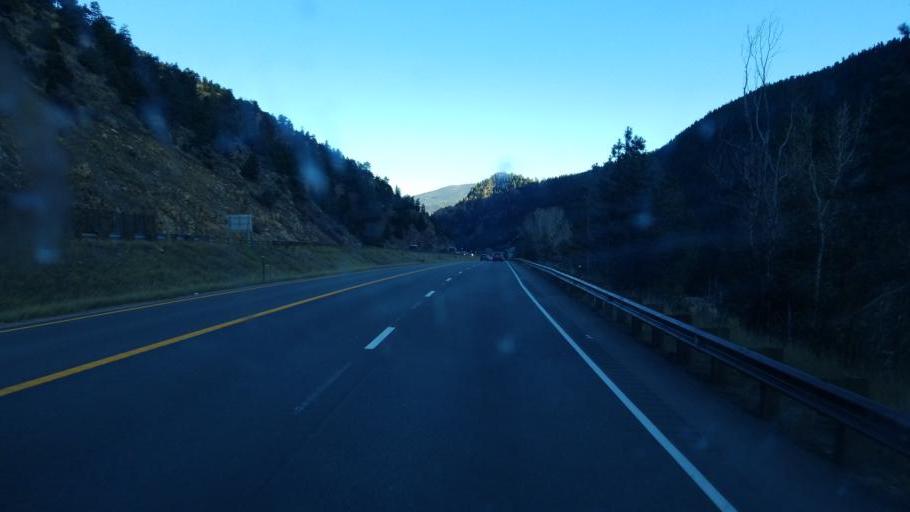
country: US
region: Colorado
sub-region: Clear Creek County
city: Idaho Springs
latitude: 39.7620
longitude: -105.5762
